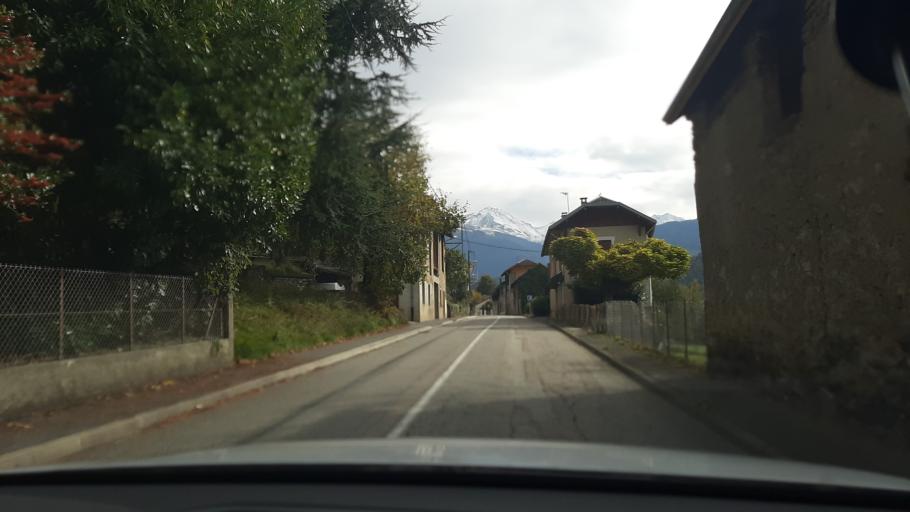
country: FR
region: Rhone-Alpes
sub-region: Departement de la Savoie
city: Montmelian
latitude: 45.4485
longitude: 6.0675
